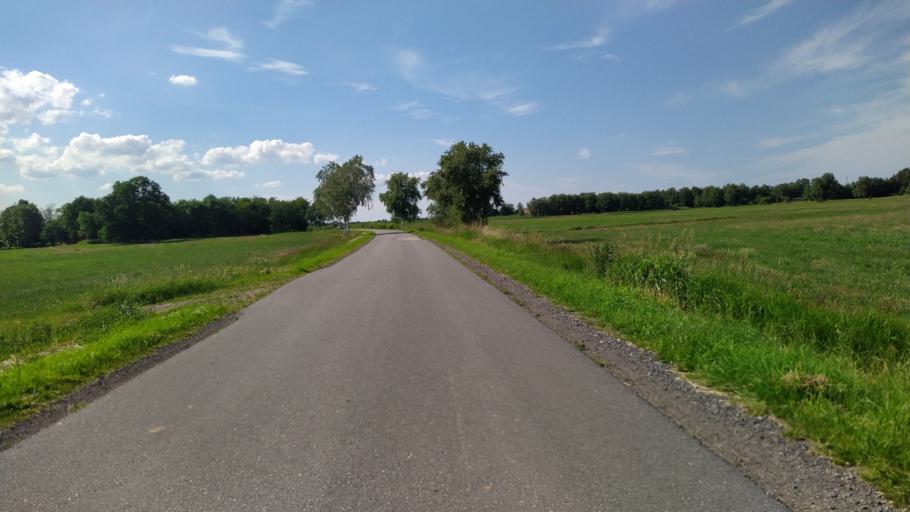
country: DE
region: Lower Saxony
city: Odisheim
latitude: 53.6684
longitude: 8.9233
